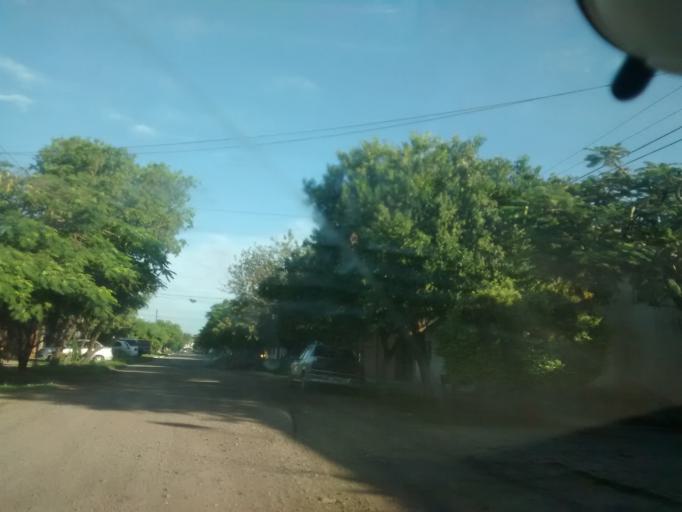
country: AR
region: Chaco
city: Resistencia
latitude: -27.4661
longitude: -58.9966
